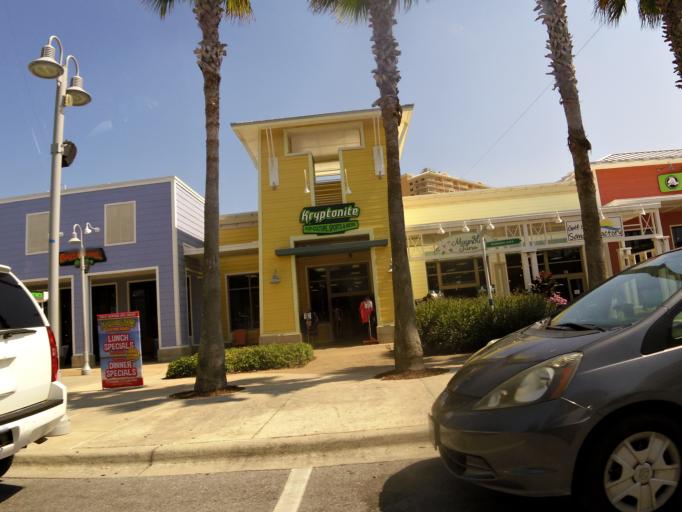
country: US
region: Florida
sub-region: Bay County
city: Laguna Beach
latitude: 30.2172
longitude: -85.8749
